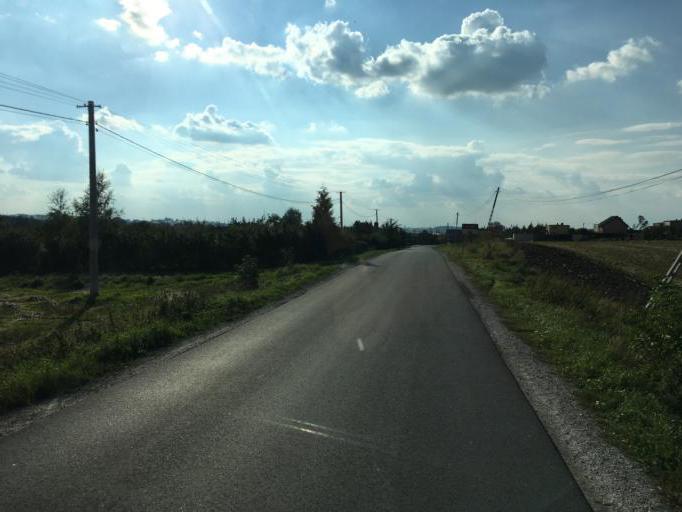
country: PL
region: Kujawsko-Pomorskie
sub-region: Powiat tucholski
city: Tuchola
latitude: 53.5934
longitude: 17.8742
